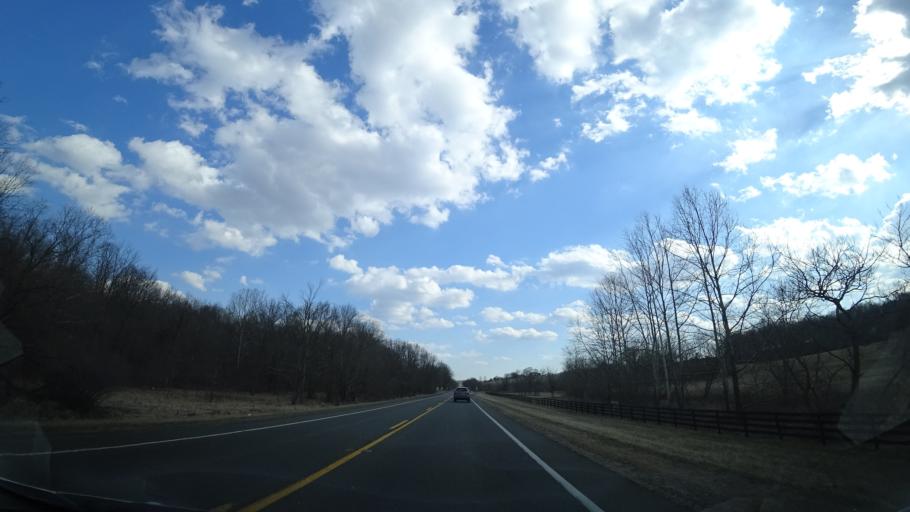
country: US
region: Virginia
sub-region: Fauquier County
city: Marshall
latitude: 38.9391
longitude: -77.9349
